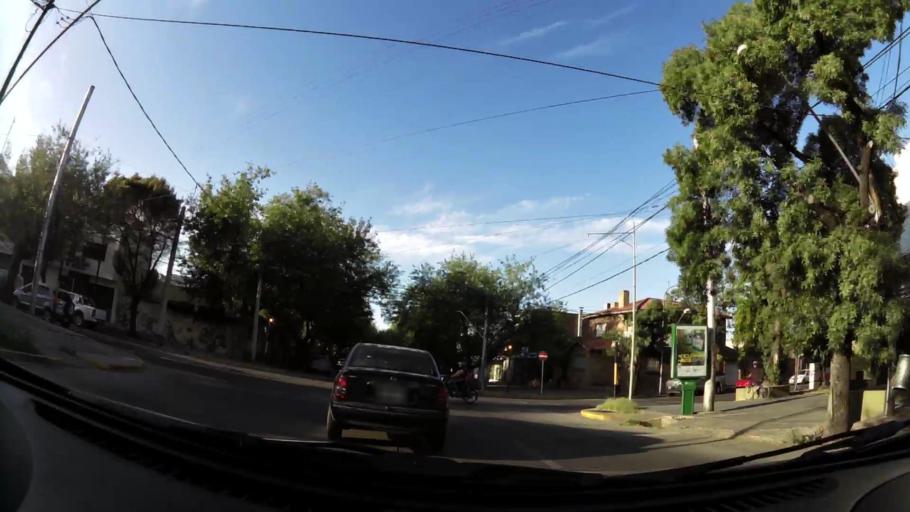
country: AR
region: Mendoza
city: Mendoza
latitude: -32.9017
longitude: -68.8409
